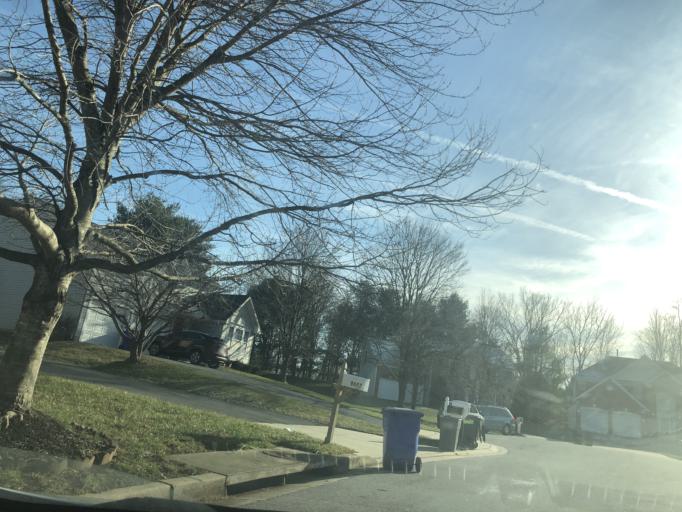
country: US
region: Maryland
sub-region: Howard County
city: Columbia
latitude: 39.2795
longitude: -76.8444
